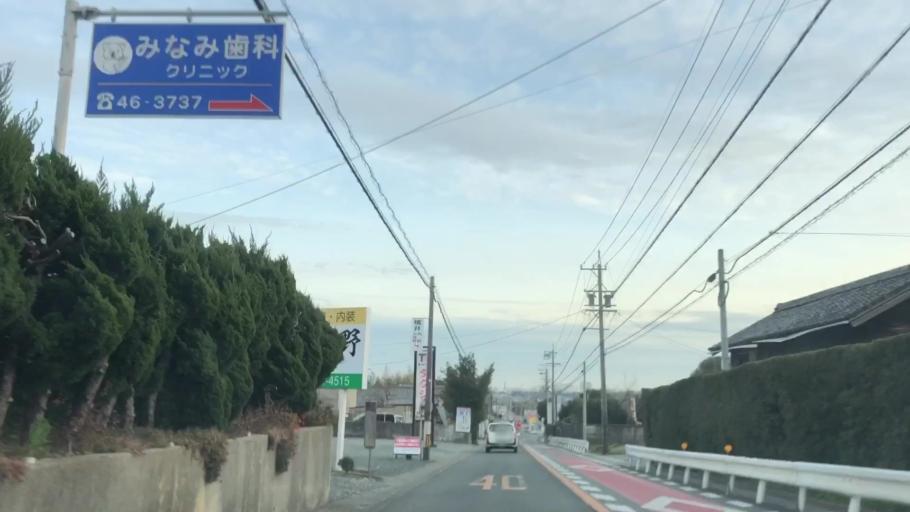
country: JP
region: Aichi
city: Toyohashi
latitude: 34.7218
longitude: 137.4039
